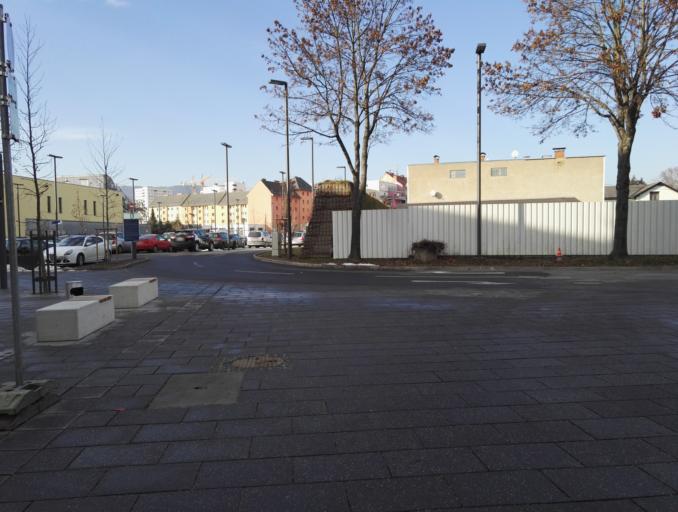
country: AT
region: Styria
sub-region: Graz Stadt
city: Graz
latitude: 47.0607
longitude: 15.4277
